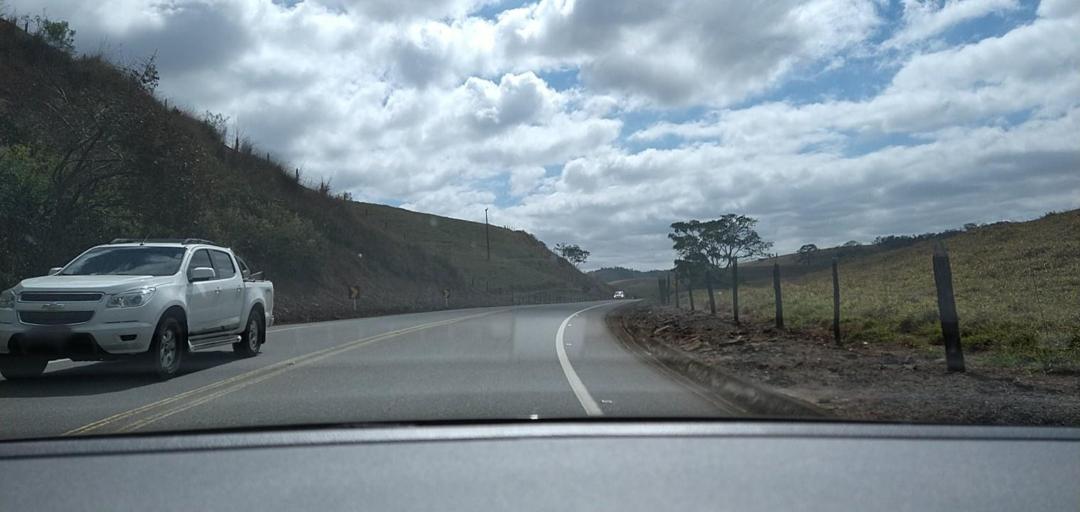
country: BR
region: Minas Gerais
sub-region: Ponte Nova
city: Ponte Nova
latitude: -20.4890
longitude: -42.8802
